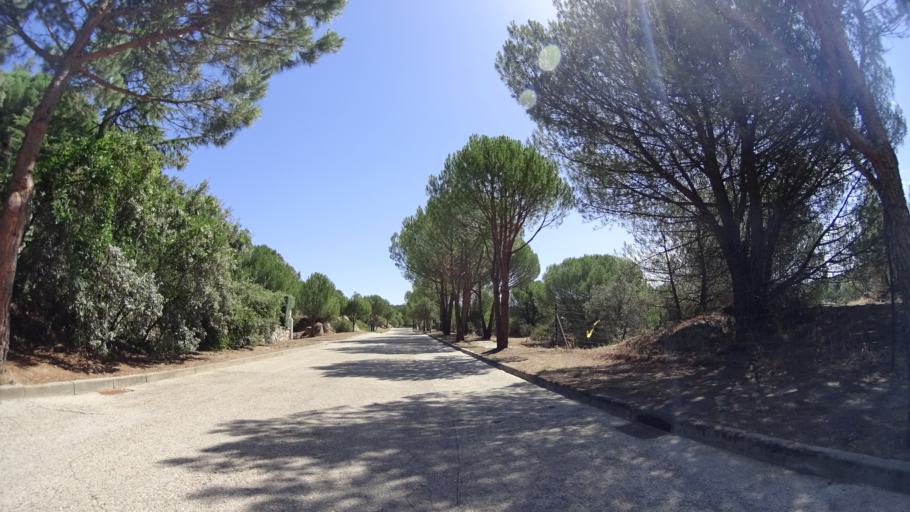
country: ES
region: Madrid
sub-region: Provincia de Madrid
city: Torrelodones
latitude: 40.5699
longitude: -3.9434
